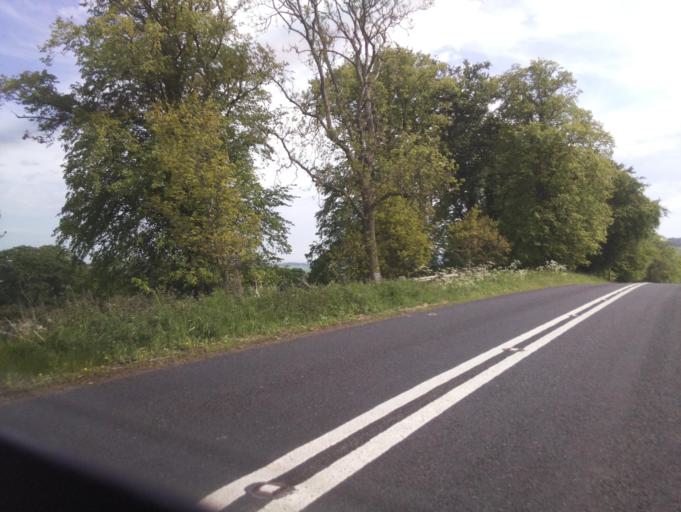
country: GB
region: England
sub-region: Northumberland
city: Alnwick
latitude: 55.4518
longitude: -1.7111
